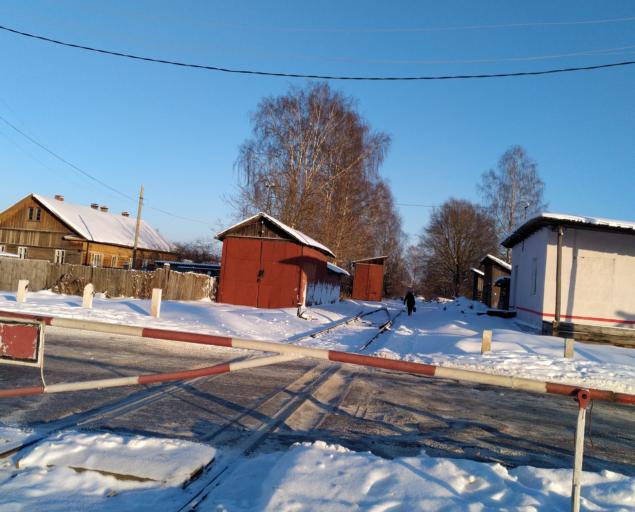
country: RU
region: Tverskaya
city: Ves'yegonsk
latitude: 58.6550
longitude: 37.2687
